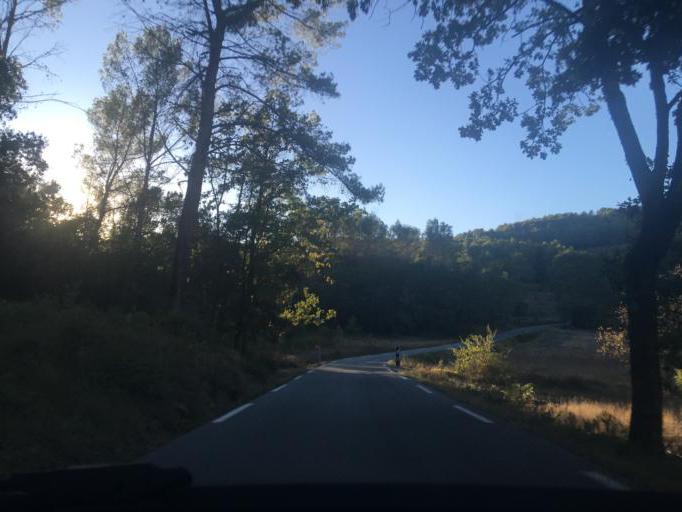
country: FR
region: Provence-Alpes-Cote d'Azur
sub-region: Departement du Var
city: Flayosc
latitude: 43.5587
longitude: 6.4066
